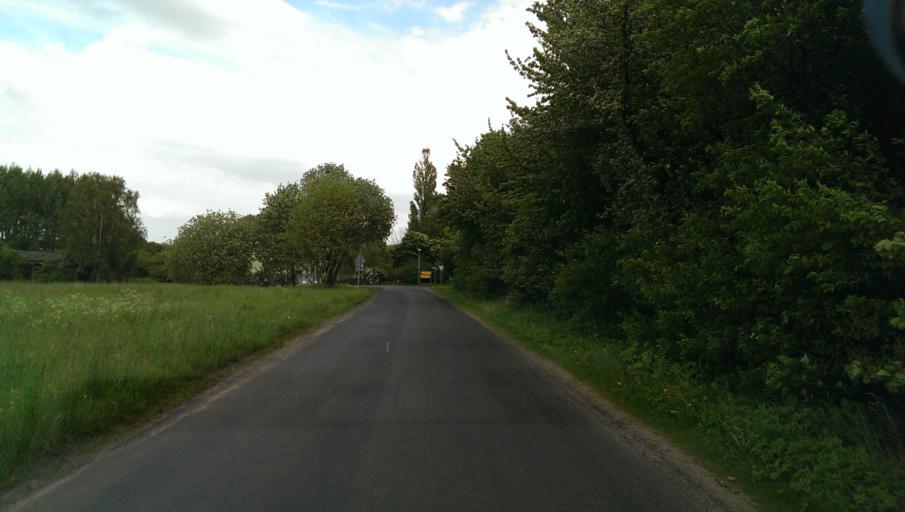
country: DE
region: Brandenburg
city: Wiesenburg
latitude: 52.1399
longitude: 12.5174
